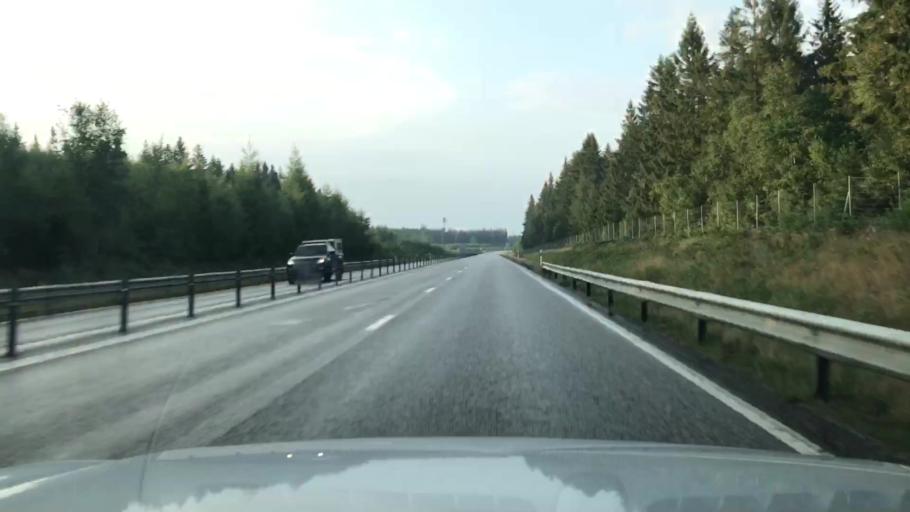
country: SE
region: Kronoberg
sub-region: Ljungby Kommun
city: Lagan
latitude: 56.9871
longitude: 14.0207
